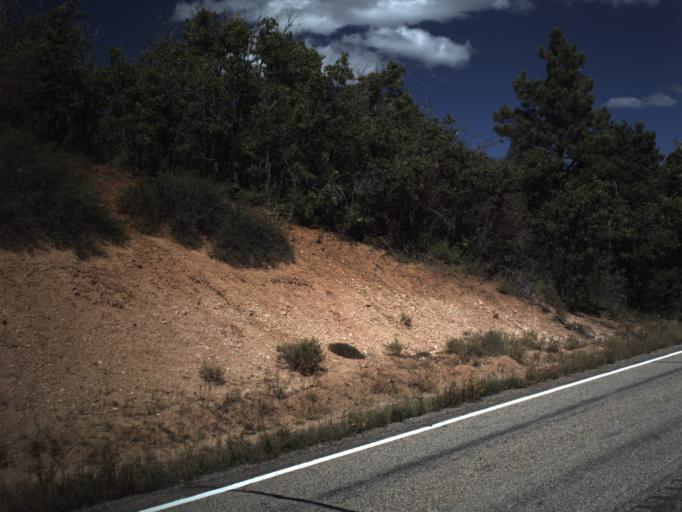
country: US
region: Utah
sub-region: Garfield County
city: Panguitch
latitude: 37.4946
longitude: -112.5546
